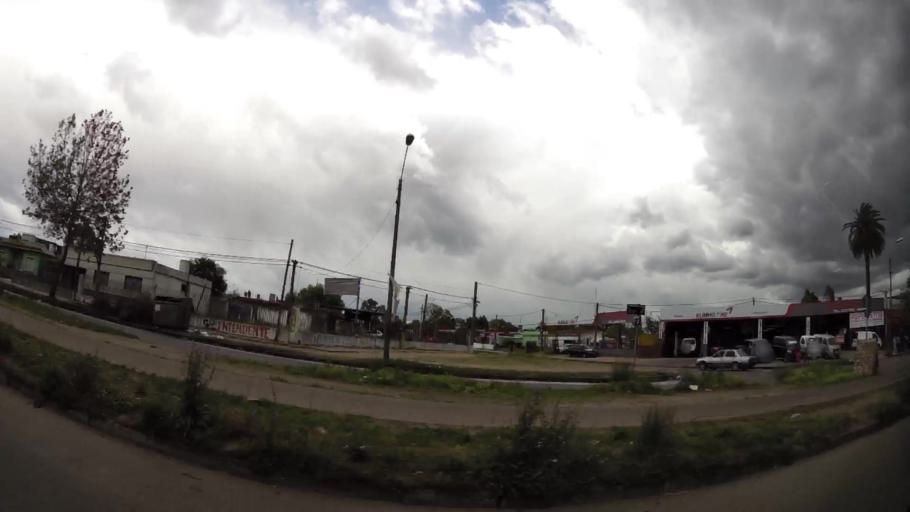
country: UY
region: Canelones
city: Toledo
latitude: -34.8193
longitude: -56.1397
